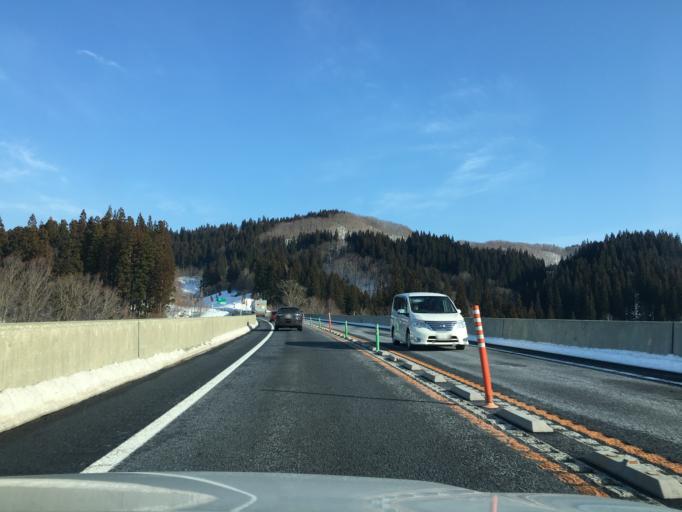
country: JP
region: Yamagata
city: Sagae
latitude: 38.4476
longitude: 139.9965
